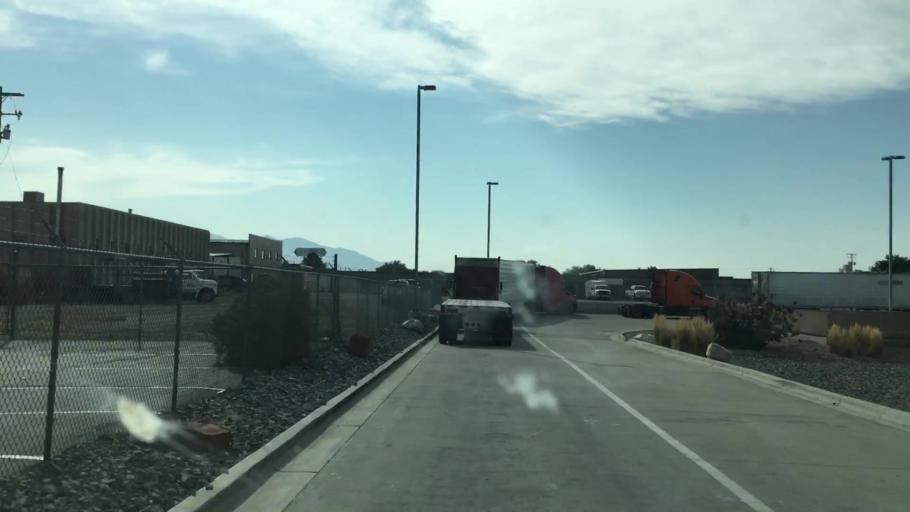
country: US
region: Utah
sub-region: Salt Lake County
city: South Salt Lake
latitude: 40.7267
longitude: -111.9174
